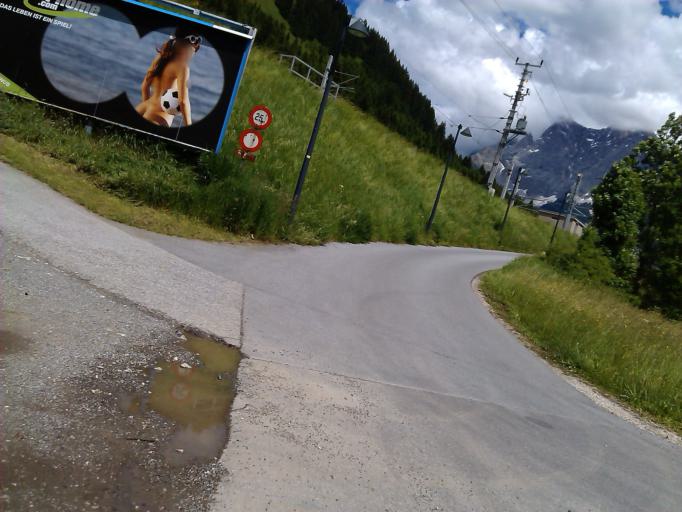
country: AT
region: Tyrol
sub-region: Politischer Bezirk Reutte
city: Lermoos
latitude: 47.4053
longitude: 10.8762
